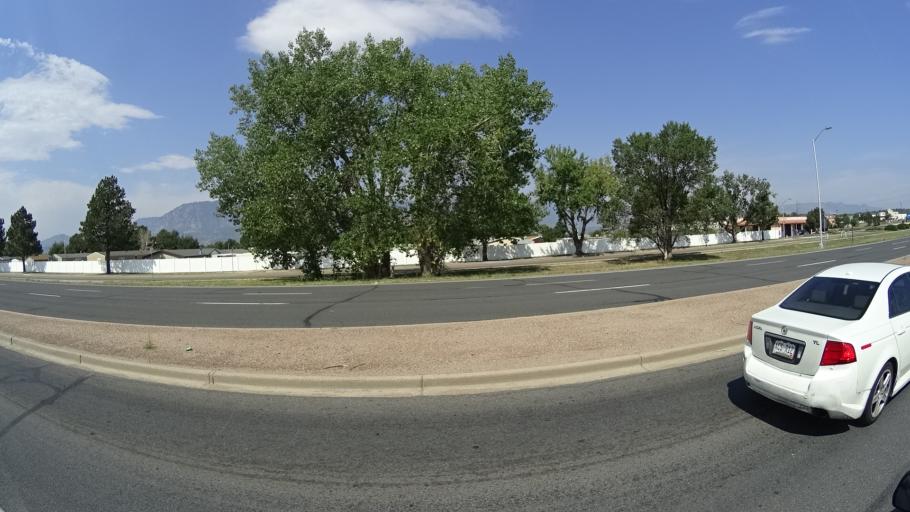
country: US
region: Colorado
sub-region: El Paso County
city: Stratmoor
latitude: 38.7857
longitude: -104.7574
